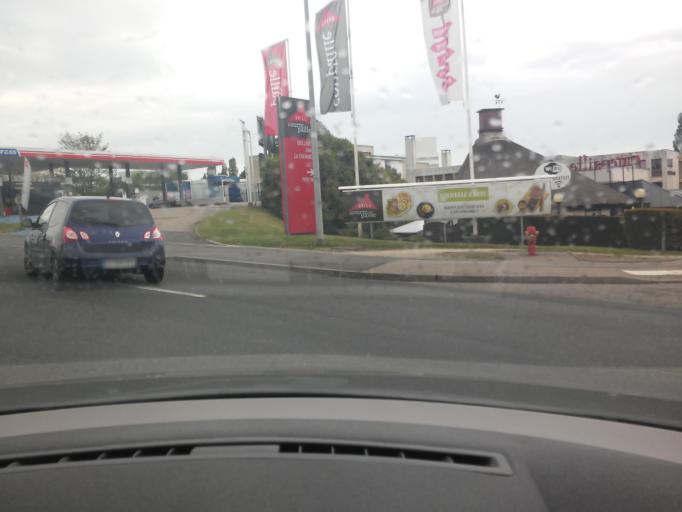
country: FR
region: Lorraine
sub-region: Departement de Meurthe-et-Moselle
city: Laxou
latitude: 48.6942
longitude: 6.1316
